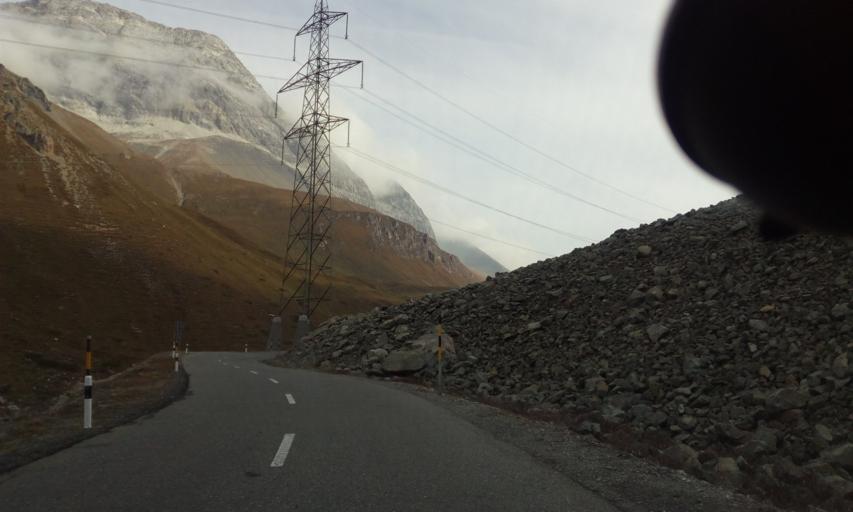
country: CH
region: Grisons
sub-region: Maloja District
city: Samedan
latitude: 46.5790
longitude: 9.8290
